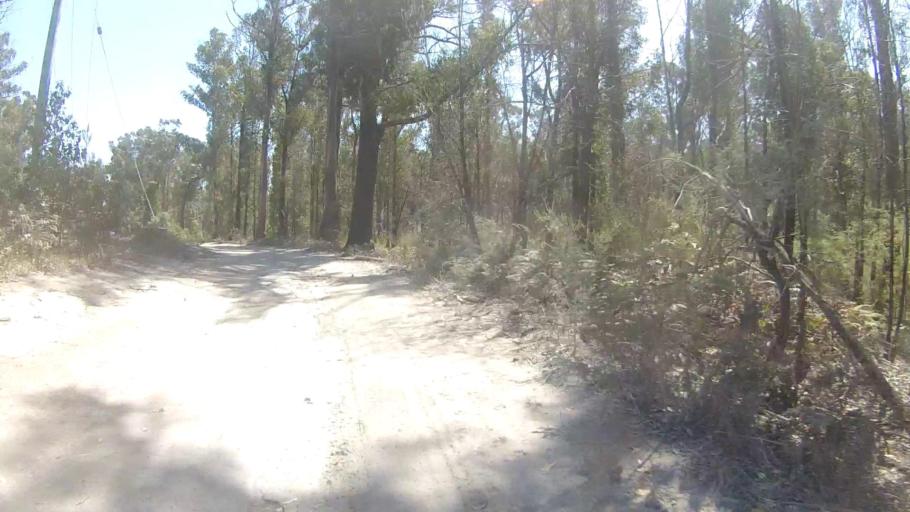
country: AU
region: Tasmania
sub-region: Sorell
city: Sorell
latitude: -42.8214
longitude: 147.6714
